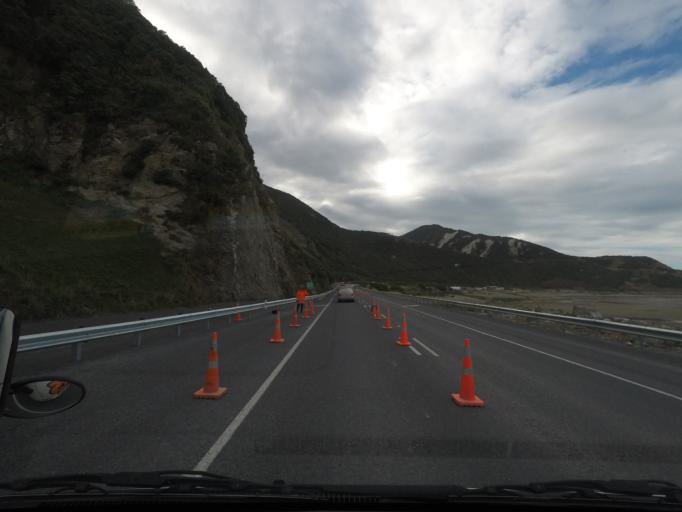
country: NZ
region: Canterbury
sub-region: Kaikoura District
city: Kaikoura
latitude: -42.2209
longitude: 173.8568
